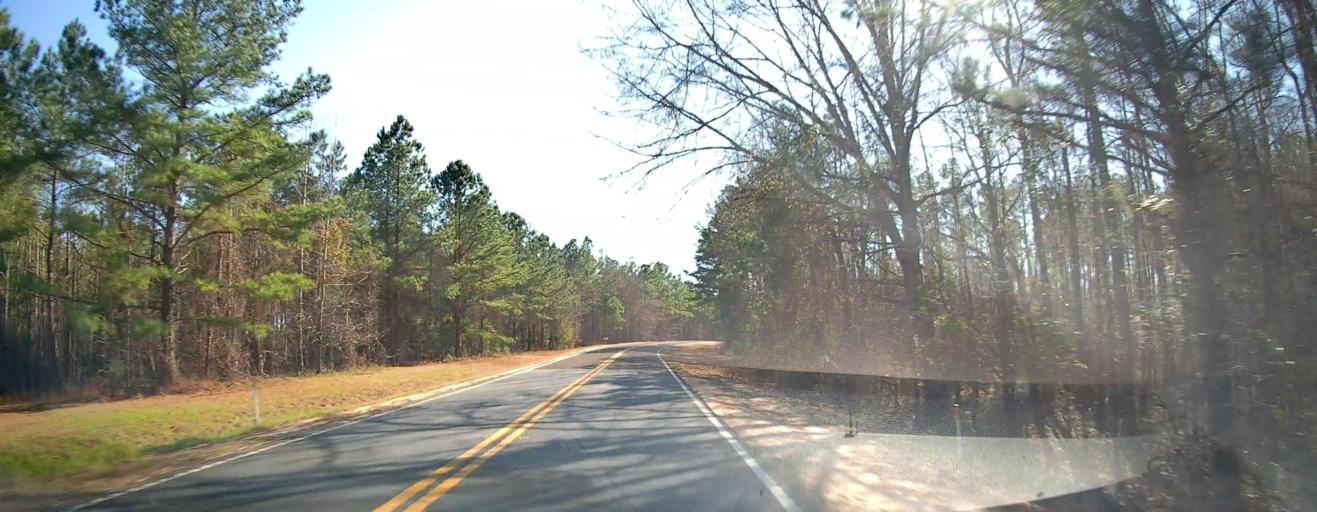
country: US
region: Georgia
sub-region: Taylor County
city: Butler
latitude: 32.6562
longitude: -84.3649
